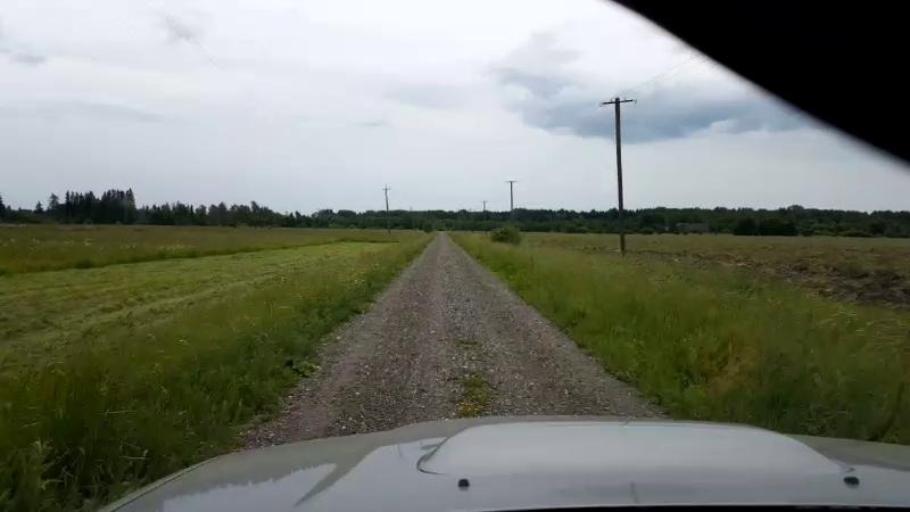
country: EE
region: Paernumaa
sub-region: Halinga vald
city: Parnu-Jaagupi
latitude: 58.5292
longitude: 24.6127
